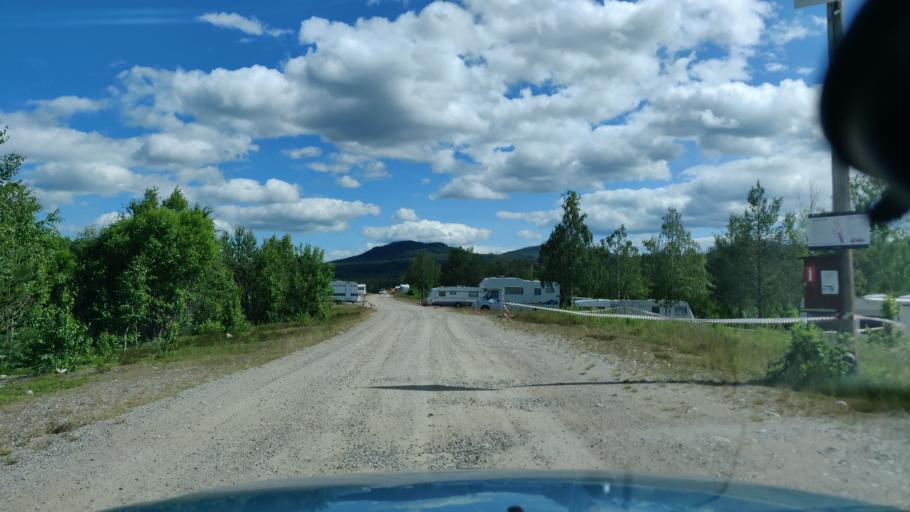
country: NO
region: Hedmark
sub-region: Trysil
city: Innbygda
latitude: 60.9118
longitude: 12.5619
